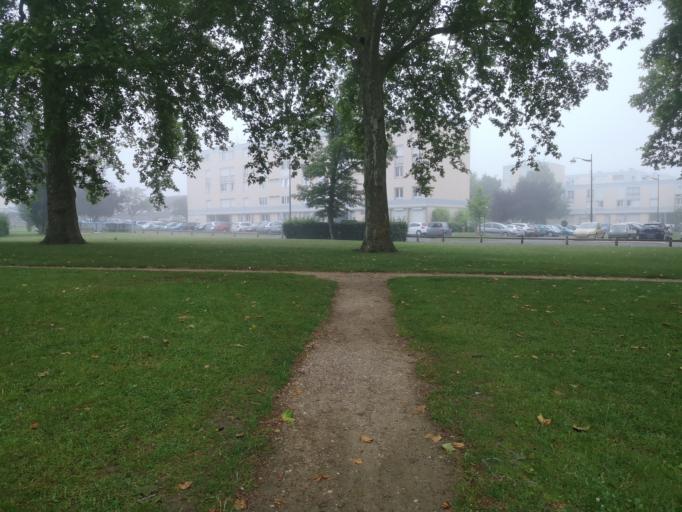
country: FR
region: Centre
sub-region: Departement du Loiret
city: Fleury-les-Aubrais
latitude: 47.9257
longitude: 1.9193
